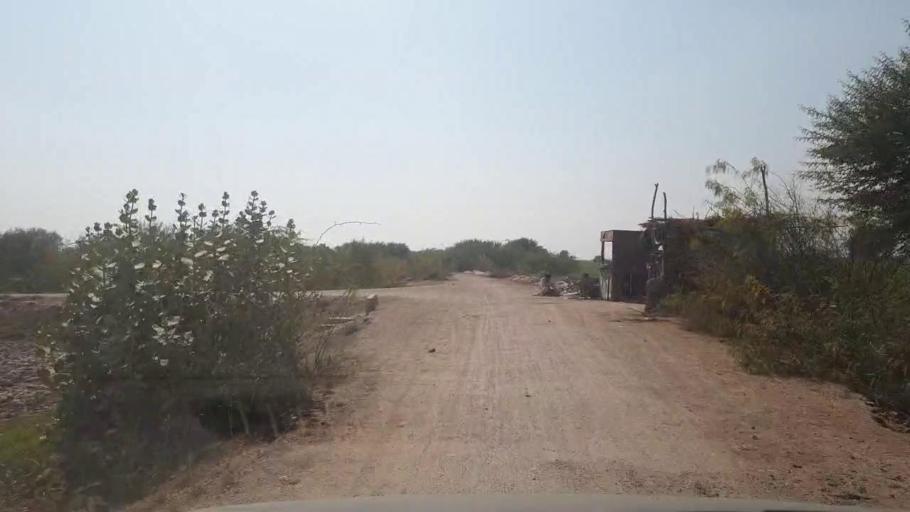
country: PK
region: Sindh
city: Chambar
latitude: 25.2269
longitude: 68.8207
